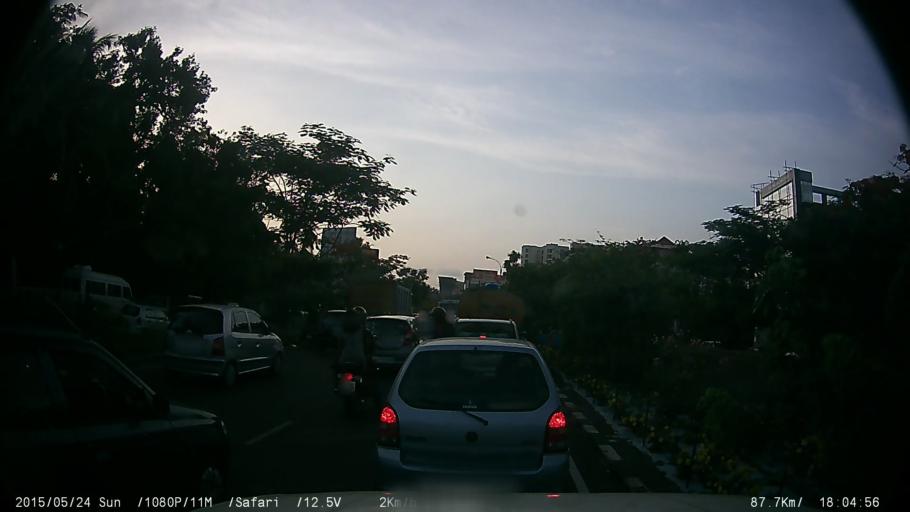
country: IN
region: Kerala
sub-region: Ernakulam
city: Elur
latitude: 10.0214
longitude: 76.3101
